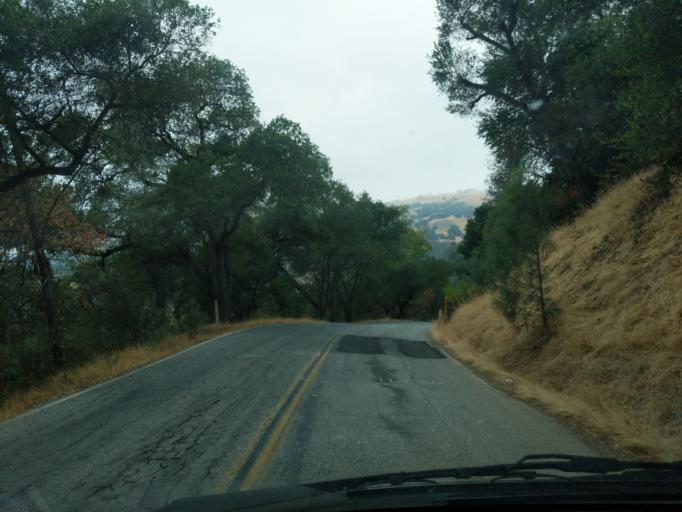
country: US
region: California
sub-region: Santa Clara County
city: Morgan Hill
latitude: 37.1486
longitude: -121.5916
